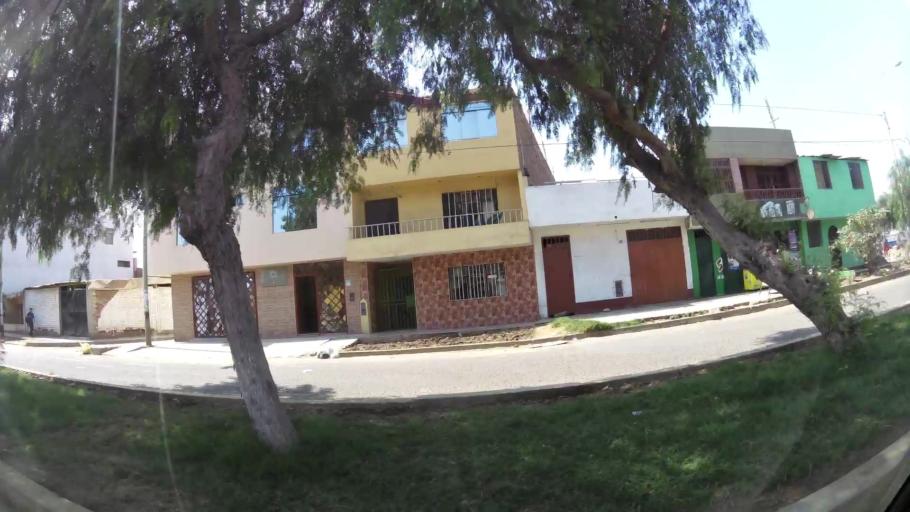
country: PE
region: La Libertad
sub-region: Provincia de Trujillo
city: Buenos Aires
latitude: -8.1338
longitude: -79.0474
